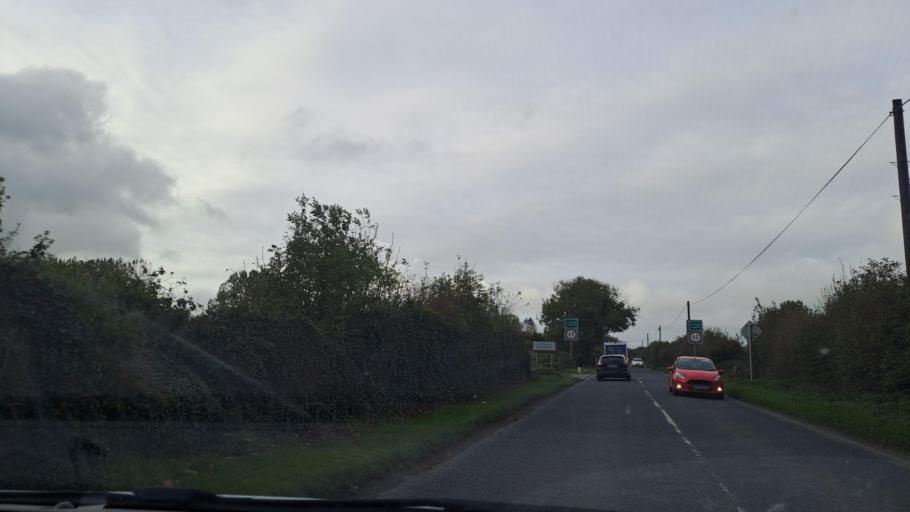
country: IE
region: Leinster
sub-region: An Mhi
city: Navan
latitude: 53.6984
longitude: -6.6787
